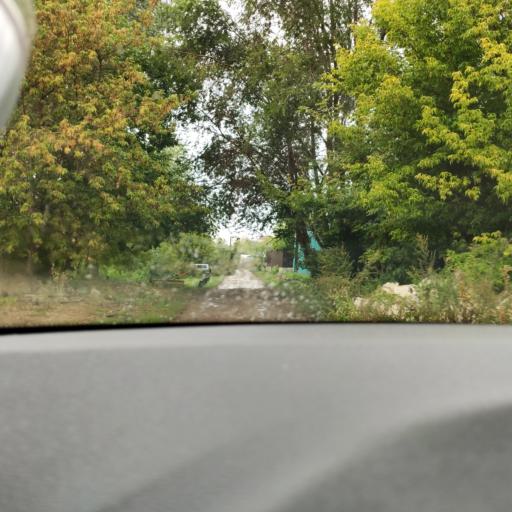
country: RU
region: Samara
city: Samara
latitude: 53.1719
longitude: 50.1590
